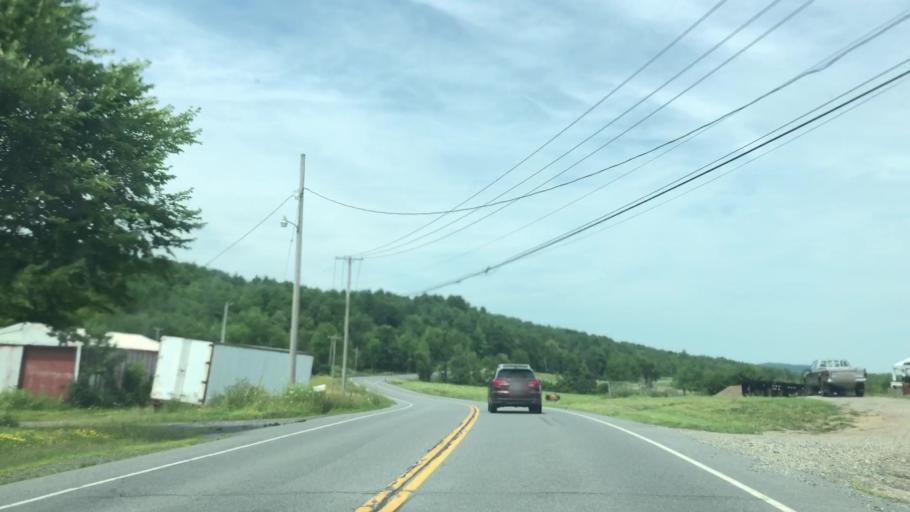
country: US
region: New York
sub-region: Washington County
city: Whitehall
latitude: 43.4915
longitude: -73.4285
